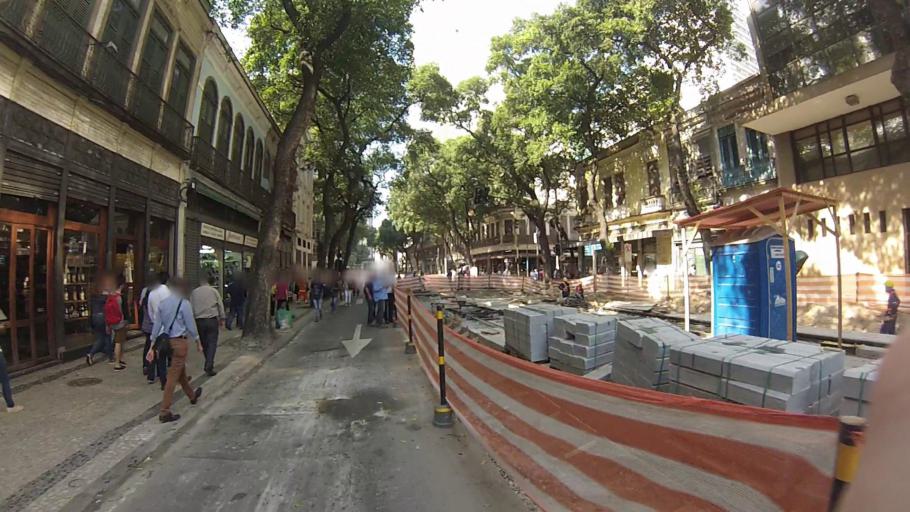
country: BR
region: Rio de Janeiro
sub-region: Rio De Janeiro
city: Rio de Janeiro
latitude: -22.9012
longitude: -43.1825
